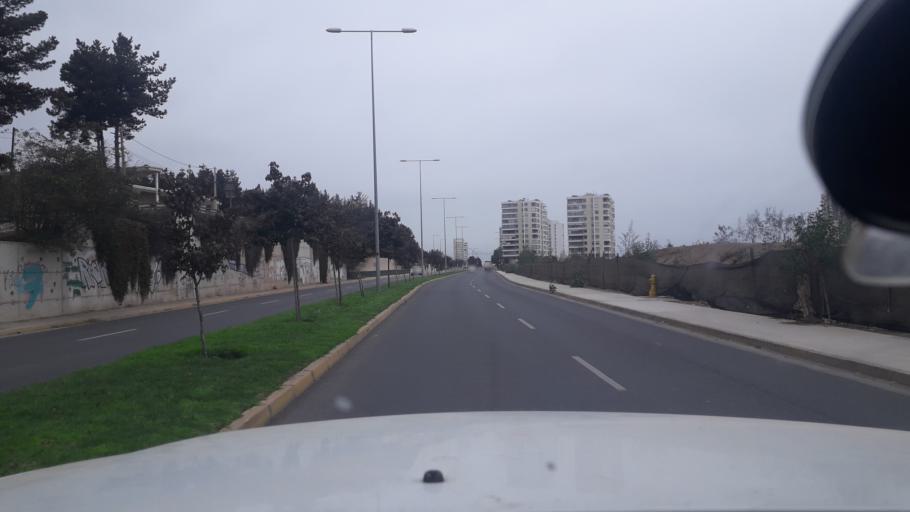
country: CL
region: Valparaiso
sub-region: Provincia de Valparaiso
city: Vina del Mar
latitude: -32.9521
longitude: -71.5388
